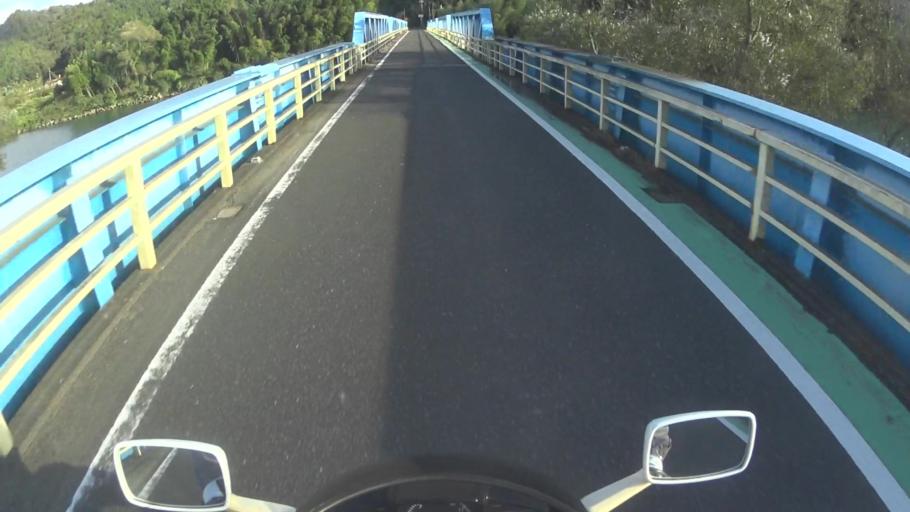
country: JP
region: Kyoto
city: Maizuru
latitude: 35.4289
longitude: 135.2542
